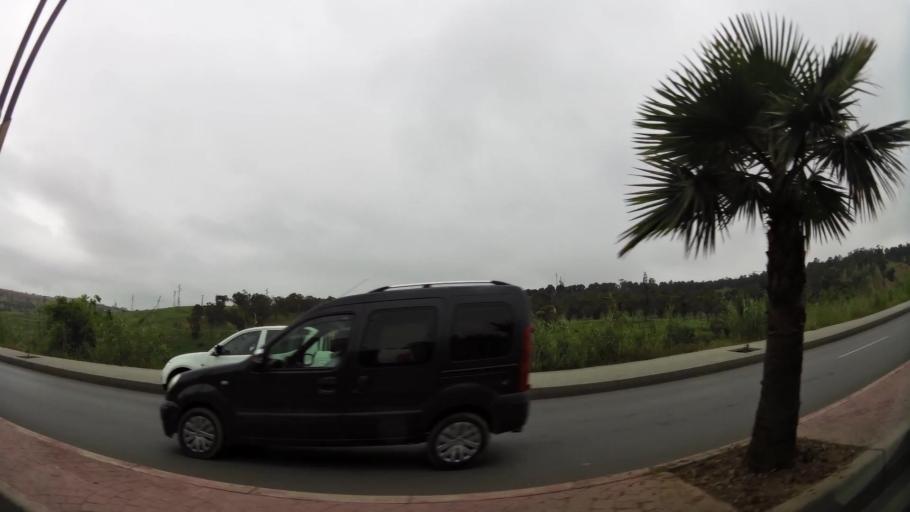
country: MA
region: Fes-Boulemane
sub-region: Fes
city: Fes
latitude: 34.0527
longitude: -4.9820
